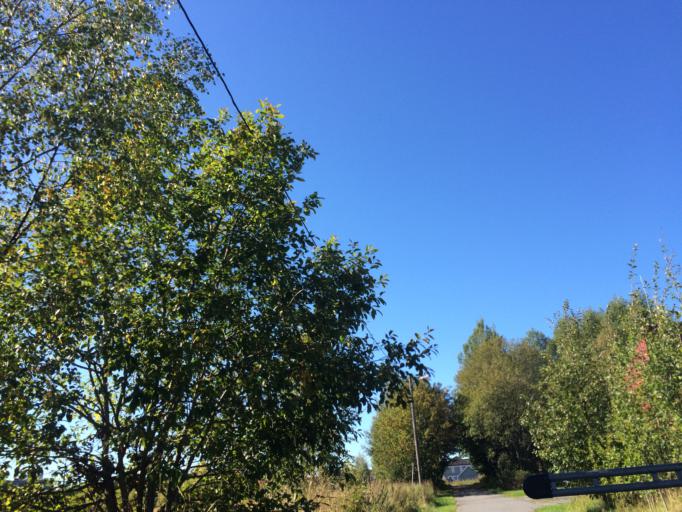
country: NO
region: Akershus
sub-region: Ski
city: Ski
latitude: 59.7142
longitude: 10.8250
